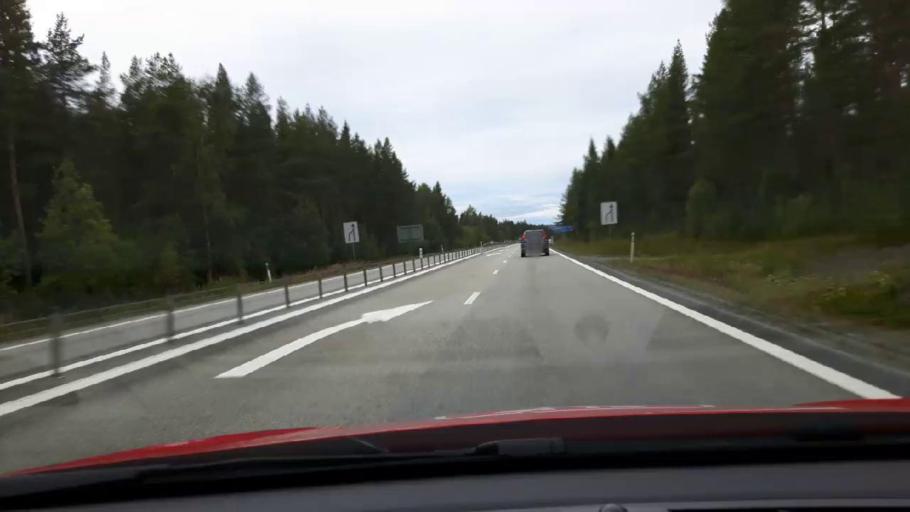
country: SE
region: Jaemtland
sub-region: OEstersunds Kommun
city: Ostersund
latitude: 63.1647
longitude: 14.7326
